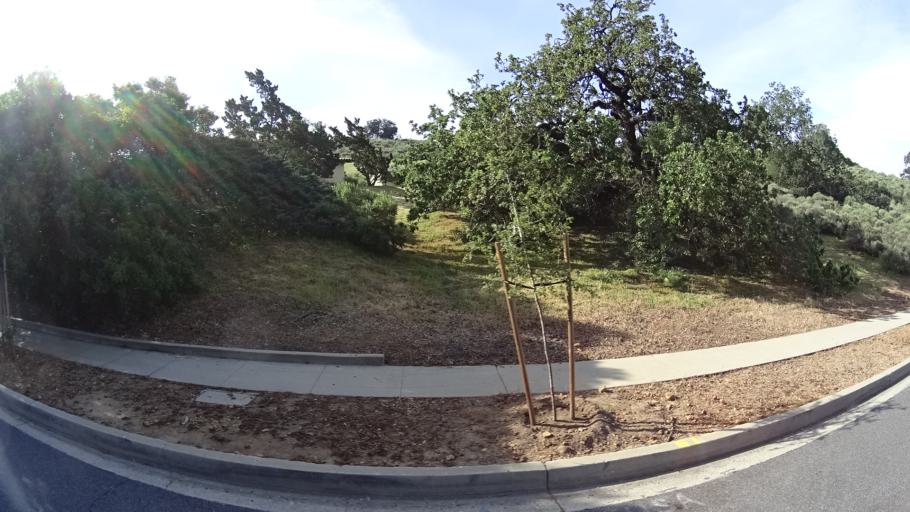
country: US
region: California
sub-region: Ventura County
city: Thousand Oaks
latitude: 34.1894
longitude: -118.8831
